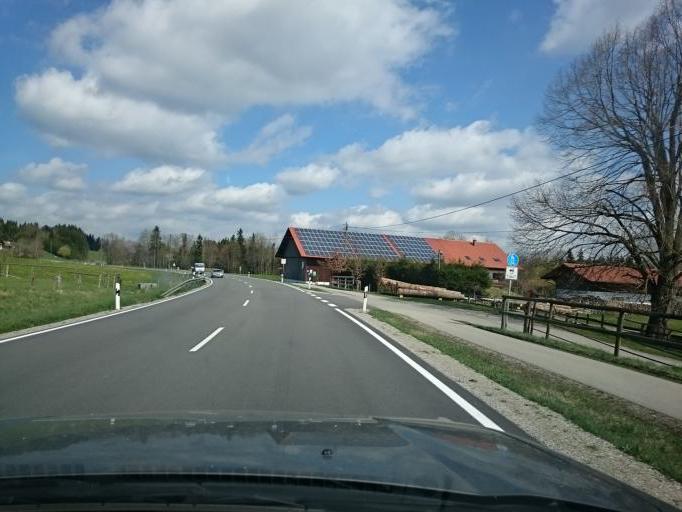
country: DE
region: Bavaria
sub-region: Upper Bavaria
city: Rottenbuch
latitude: 47.7151
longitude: 10.9742
